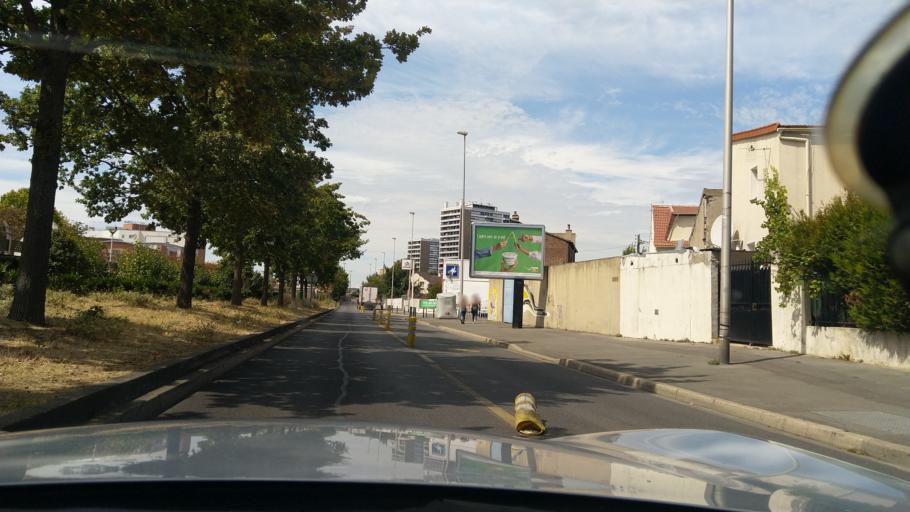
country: FR
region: Ile-de-France
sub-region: Departement de Seine-Saint-Denis
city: Bobigny
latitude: 48.9116
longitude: 2.4407
